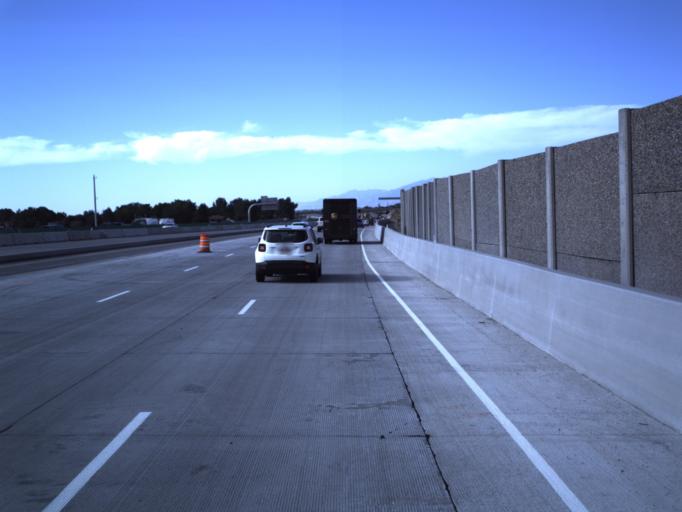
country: US
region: Utah
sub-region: Salt Lake County
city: Taylorsville
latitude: 40.6754
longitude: -111.9523
